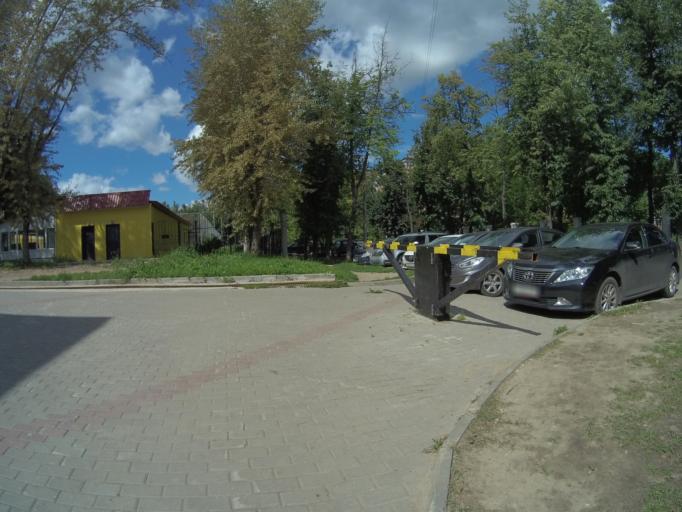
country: RU
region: Vladimir
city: Vladimir
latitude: 56.1427
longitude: 40.4164
